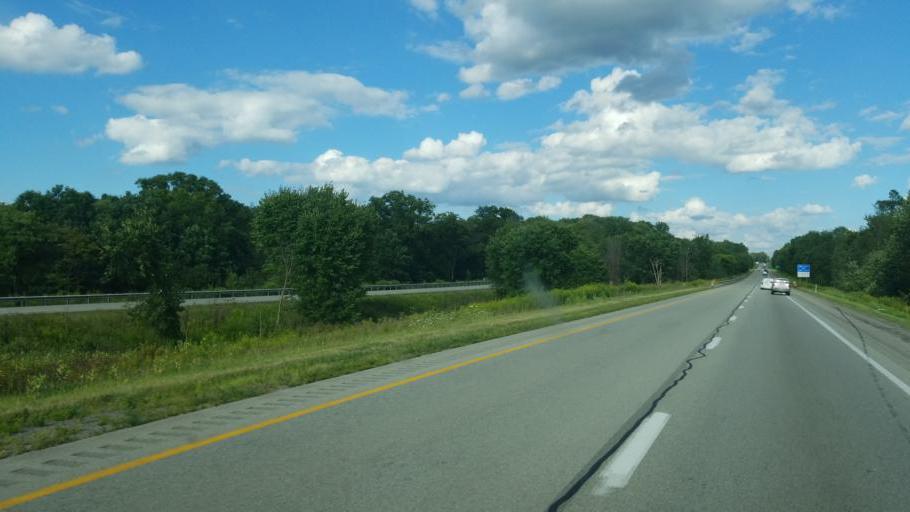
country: US
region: Pennsylvania
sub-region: Mercer County
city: Grove City
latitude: 41.2011
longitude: -80.0132
